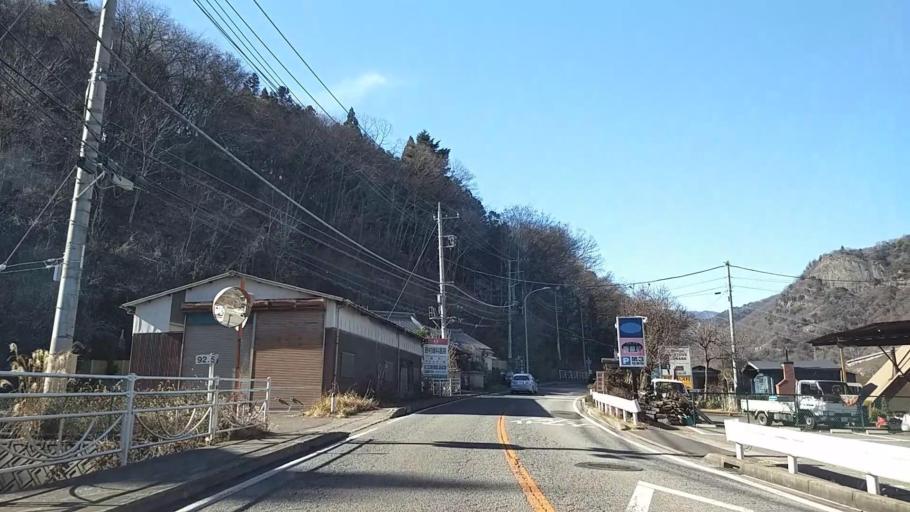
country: JP
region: Yamanashi
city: Otsuki
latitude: 35.6114
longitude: 138.9610
